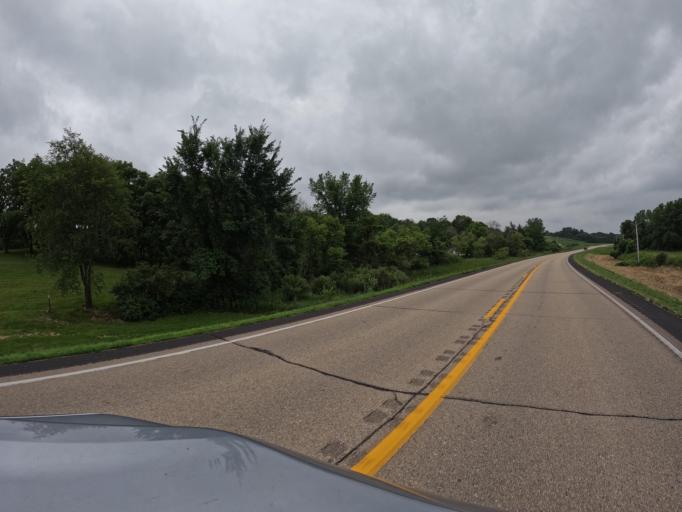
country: US
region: Illinois
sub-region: Carroll County
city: Savanna
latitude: 42.0209
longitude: -90.1832
